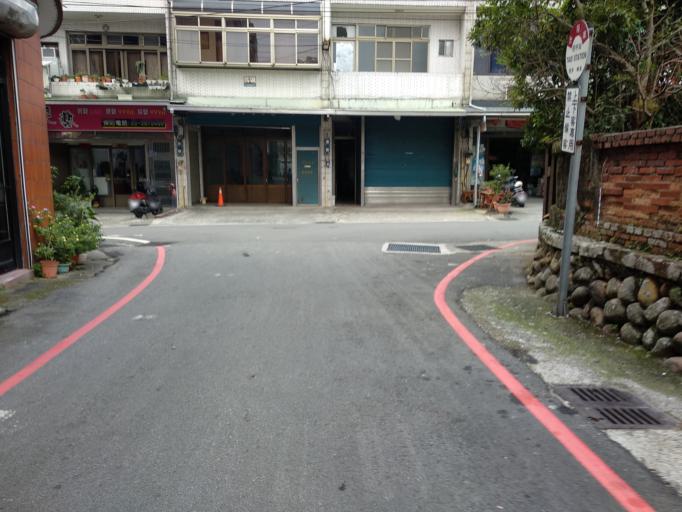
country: TW
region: Taiwan
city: Daxi
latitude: 24.7898
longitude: 121.1768
